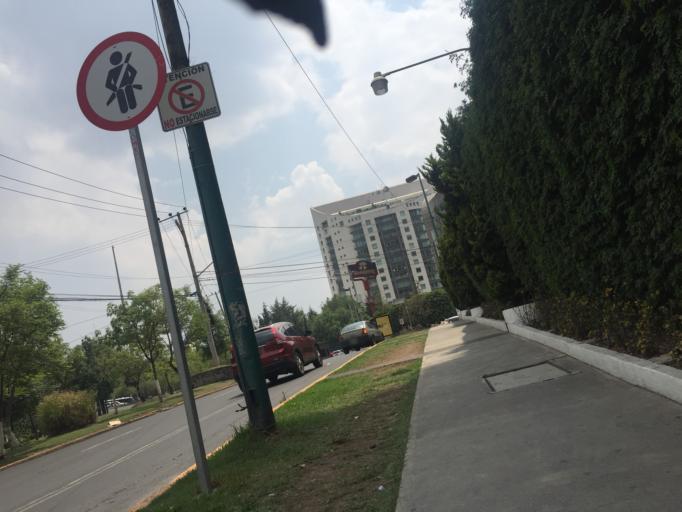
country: MX
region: Mexico City
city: Col. Bosques de las Lomas
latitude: 19.3845
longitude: -99.2656
